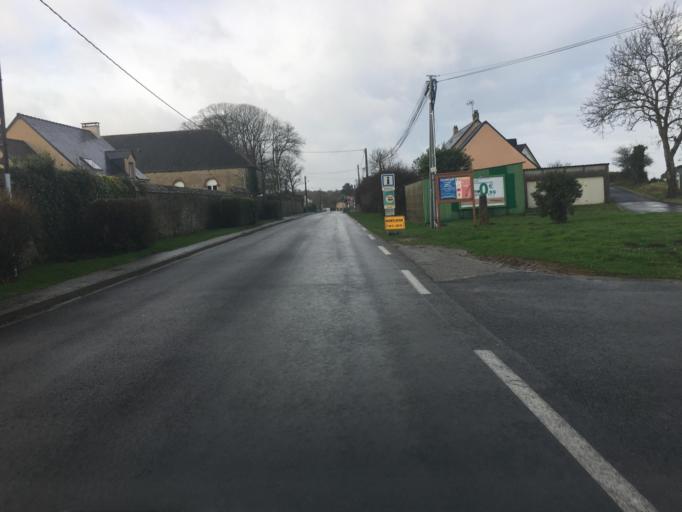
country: FR
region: Lower Normandy
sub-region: Departement de la Manche
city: Saint-Pierre-Eglise
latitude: 49.6671
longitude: -1.3941
